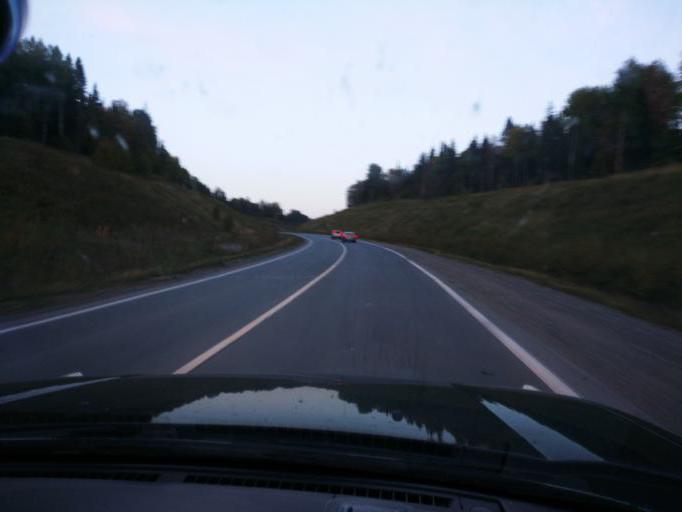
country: RU
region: Perm
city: Sylva
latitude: 58.2958
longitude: 56.8050
